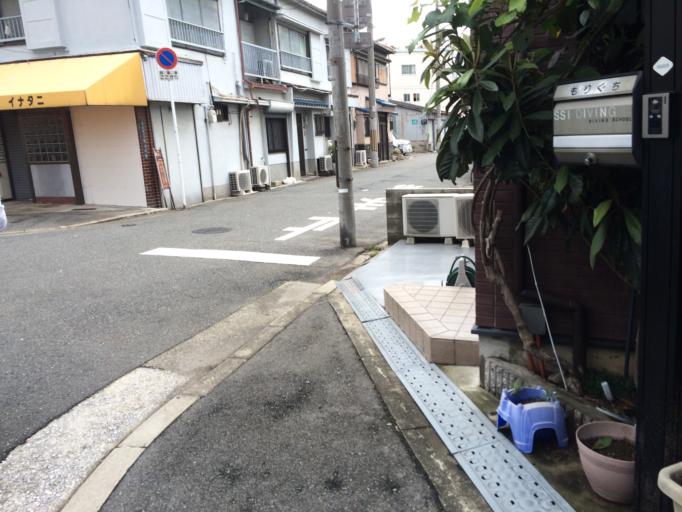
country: JP
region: Osaka
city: Sakai
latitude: 34.5955
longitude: 135.5071
